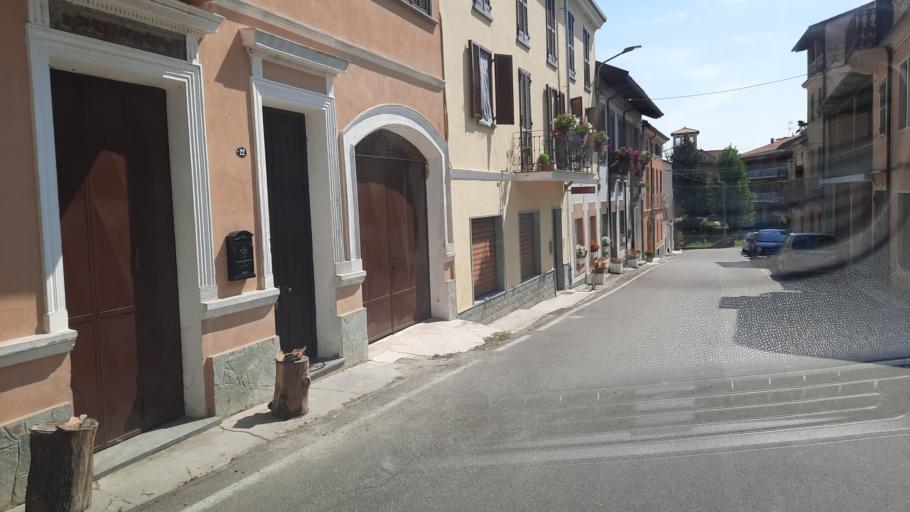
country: IT
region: Piedmont
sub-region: Provincia di Alessandria
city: Gabiano
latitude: 45.1590
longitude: 8.1935
